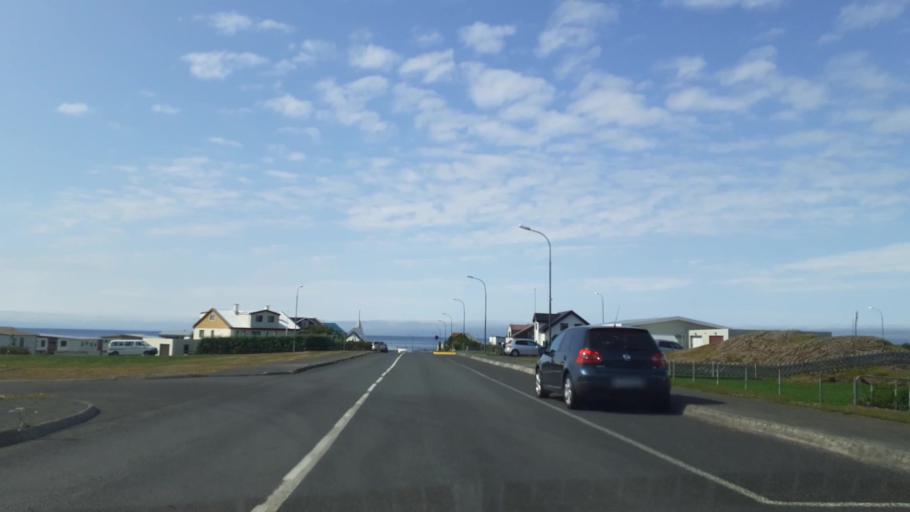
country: IS
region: Northwest
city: Saudarkrokur
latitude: 65.8237
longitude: -20.2976
